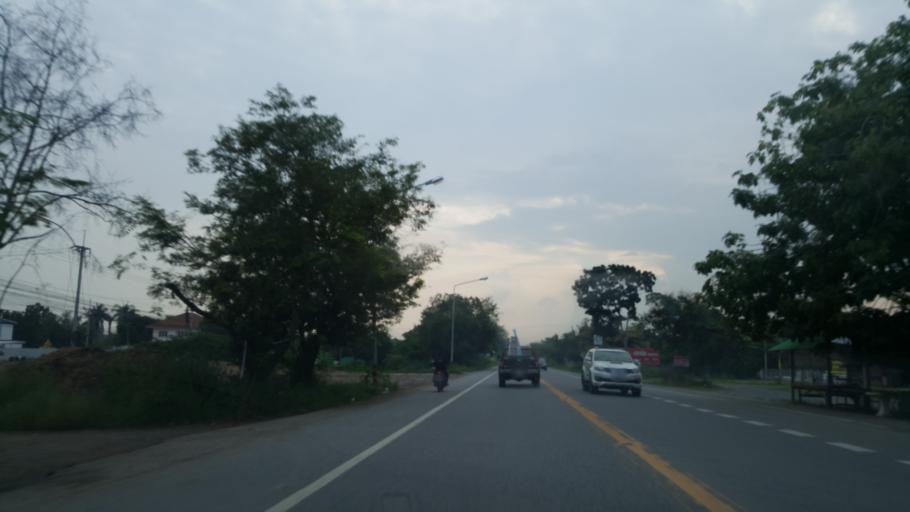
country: TH
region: Rayong
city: Ban Chang
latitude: 12.7270
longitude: 100.9709
